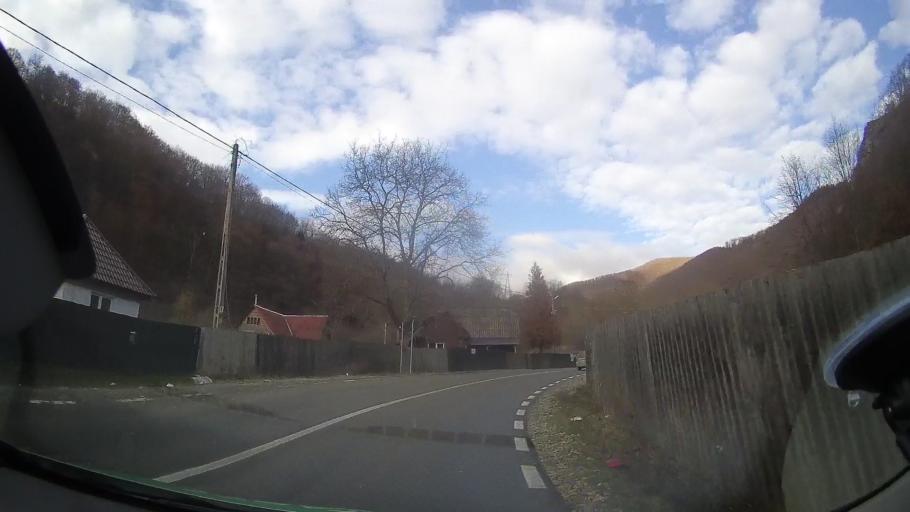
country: RO
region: Cluj
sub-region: Comuna Baisoara
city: Baisoara
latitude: 46.6056
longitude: 23.4191
